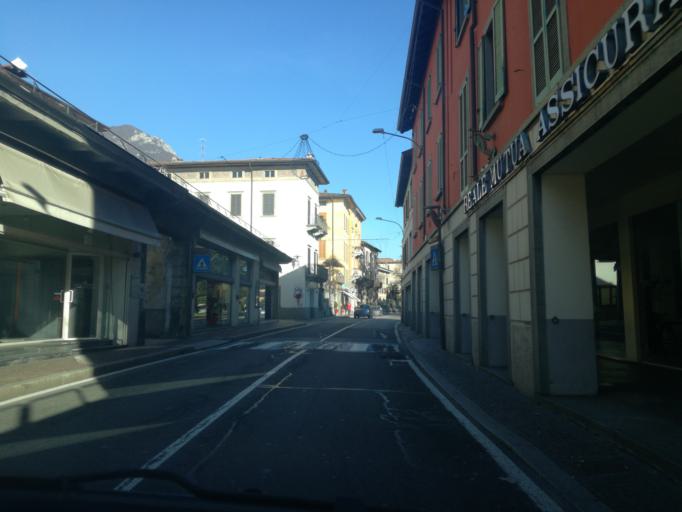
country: IT
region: Lombardy
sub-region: Provincia di Bergamo
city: Lovere
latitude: 45.8173
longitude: 10.0762
